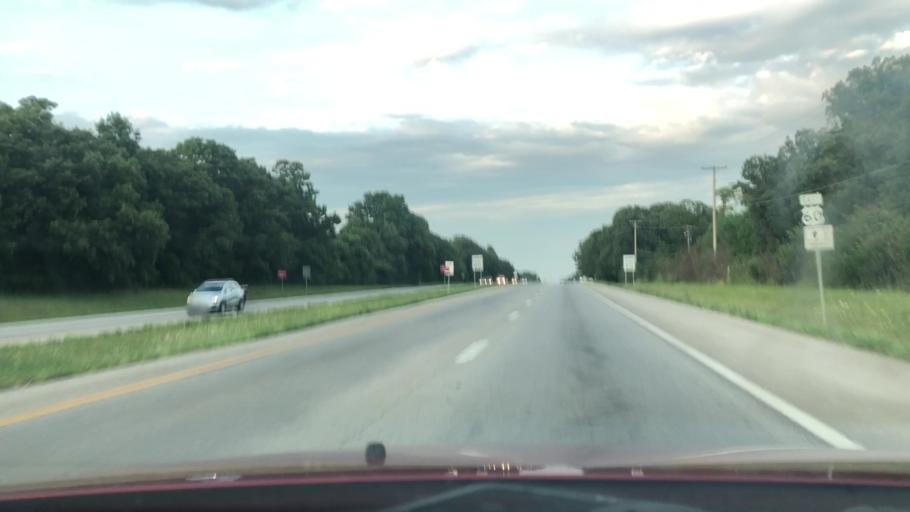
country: US
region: Missouri
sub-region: Greene County
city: Republic
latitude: 37.1368
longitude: -93.4495
